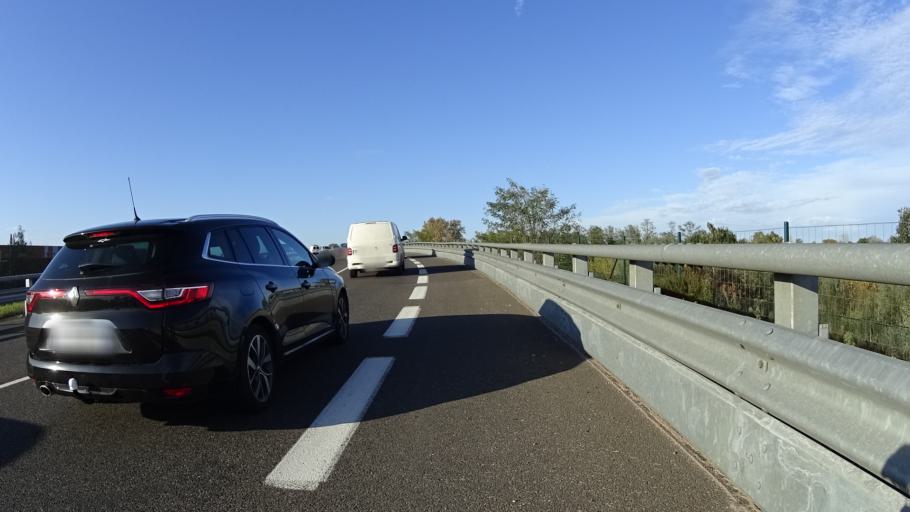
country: FR
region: Aquitaine
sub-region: Departement des Landes
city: Saint-Paul-les-Dax
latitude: 43.7262
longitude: -1.0356
